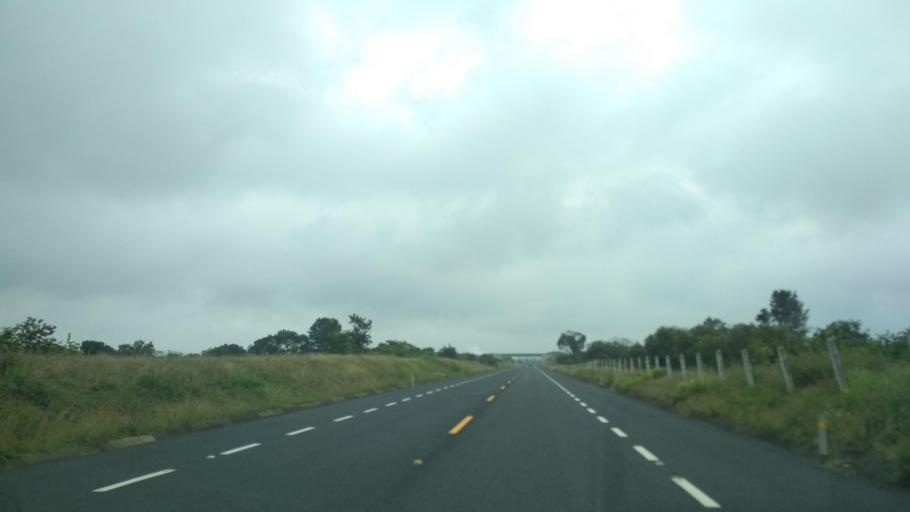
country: MX
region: Veracruz
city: Vega de San Marcos
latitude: 20.1945
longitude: -96.9727
